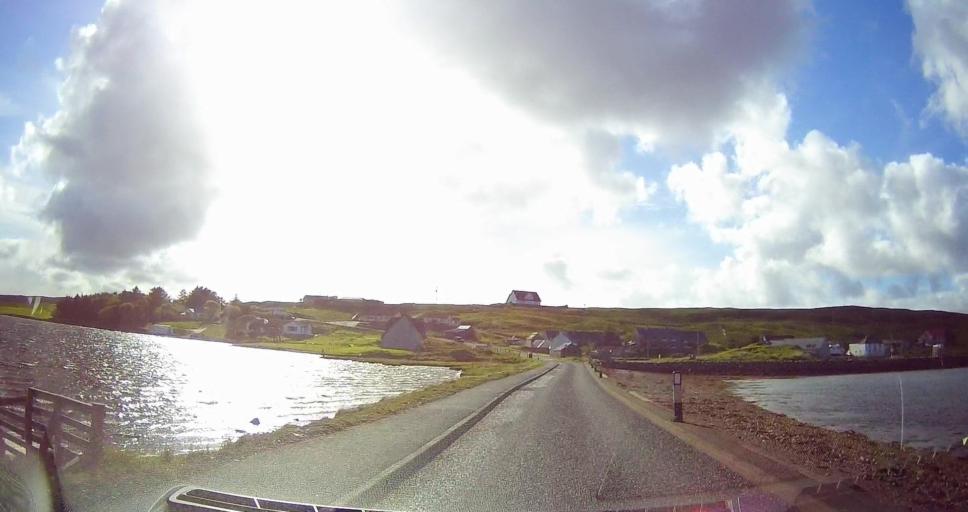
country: GB
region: Scotland
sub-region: Shetland Islands
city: Shetland
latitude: 60.3694
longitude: -1.1301
